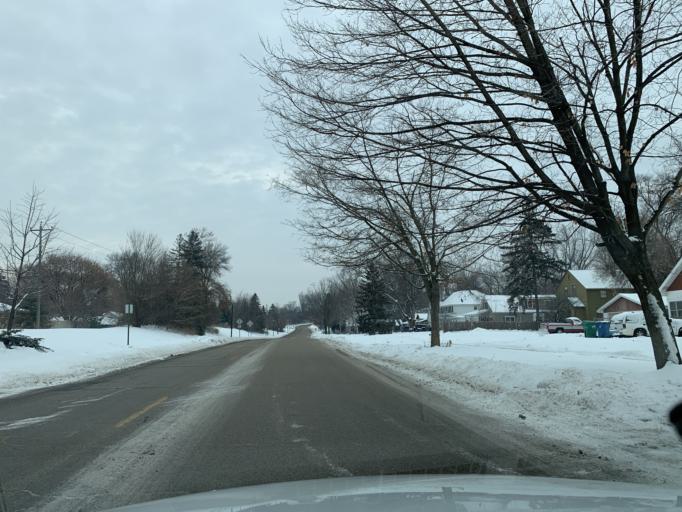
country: US
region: Minnesota
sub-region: Hennepin County
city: Edina
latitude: 44.9167
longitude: -93.3538
